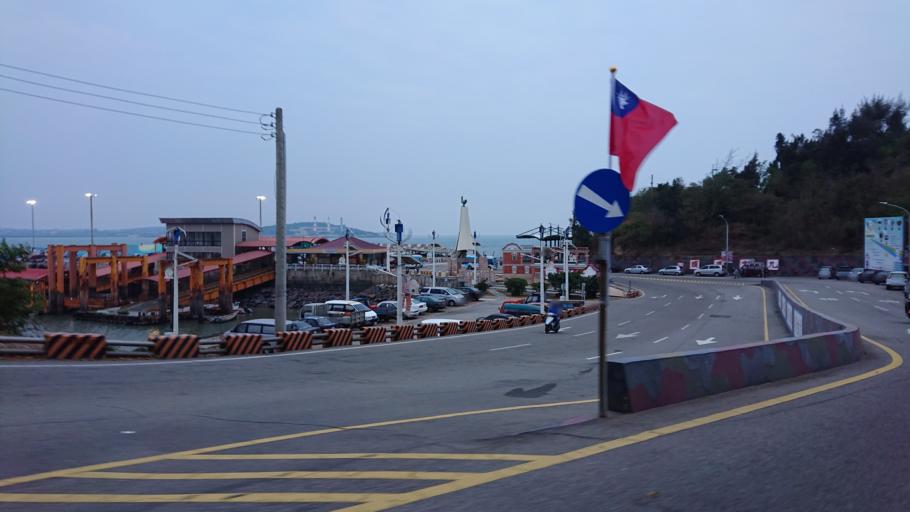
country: TW
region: Fukien
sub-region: Kinmen
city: Jincheng
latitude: 24.4262
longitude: 118.2622
